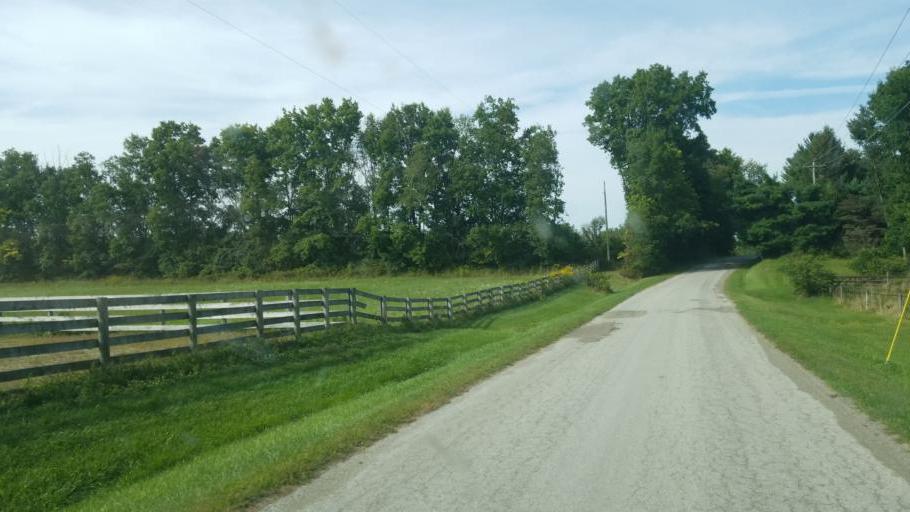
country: US
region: Ohio
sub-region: Knox County
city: Centerburg
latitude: 40.4173
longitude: -82.6509
